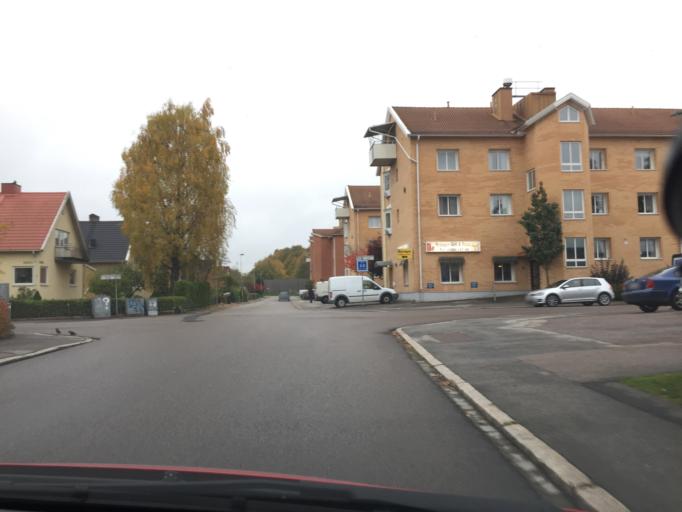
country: SE
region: Vaestra Goetaland
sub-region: Trollhattan
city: Trollhattan
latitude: 58.2845
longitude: 12.3103
